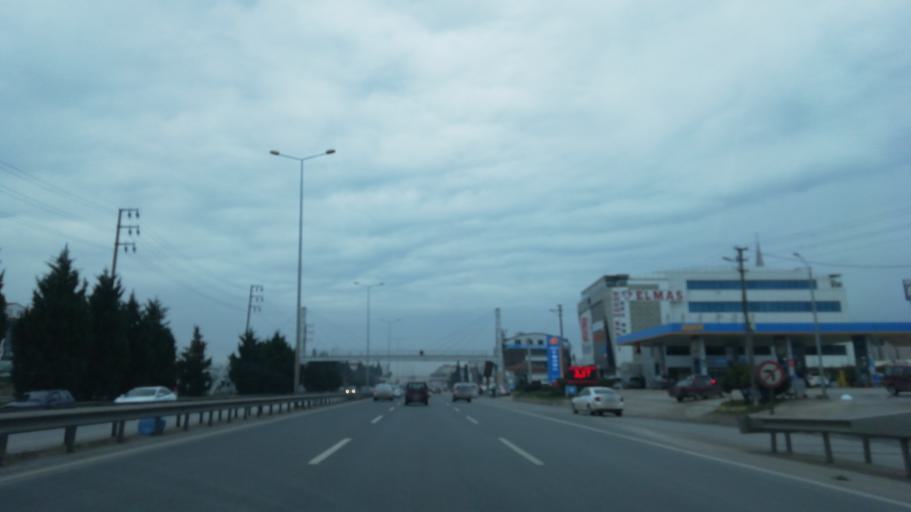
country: TR
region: Kocaeli
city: Derince
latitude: 40.7575
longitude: 29.8026
